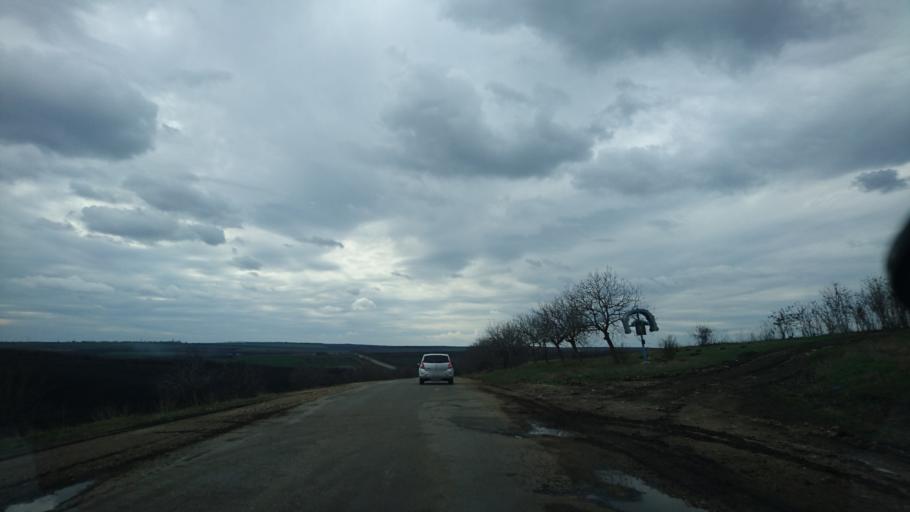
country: MD
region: Gagauzia
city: Comrat
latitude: 46.3100
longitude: 28.5939
